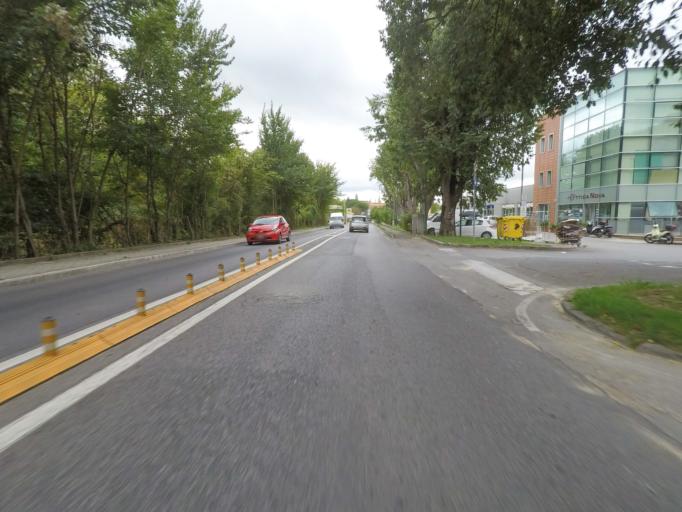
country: IT
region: Tuscany
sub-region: Provincia di Siena
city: Siena
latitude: 43.3229
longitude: 11.3473
